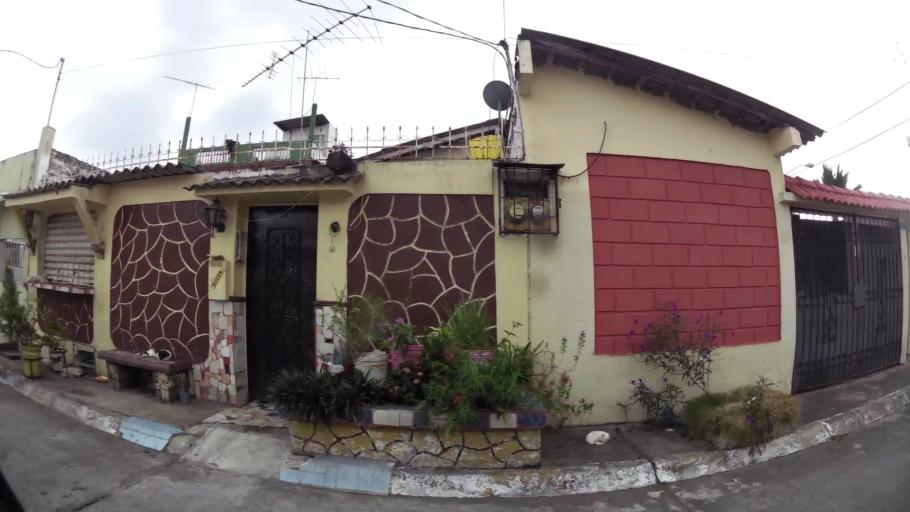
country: EC
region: Guayas
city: Eloy Alfaro
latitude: -2.1201
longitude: -79.8852
